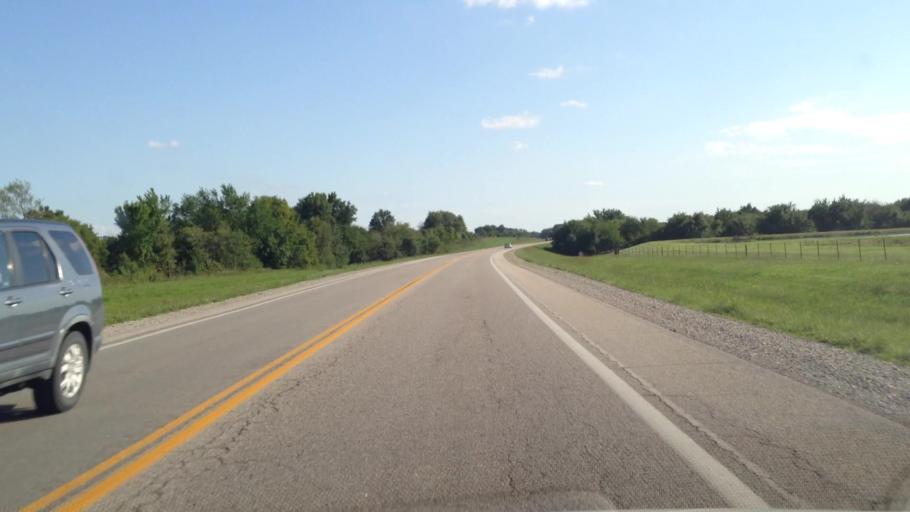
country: US
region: Kansas
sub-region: Crawford County
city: Arma
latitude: 37.5390
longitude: -94.7099
